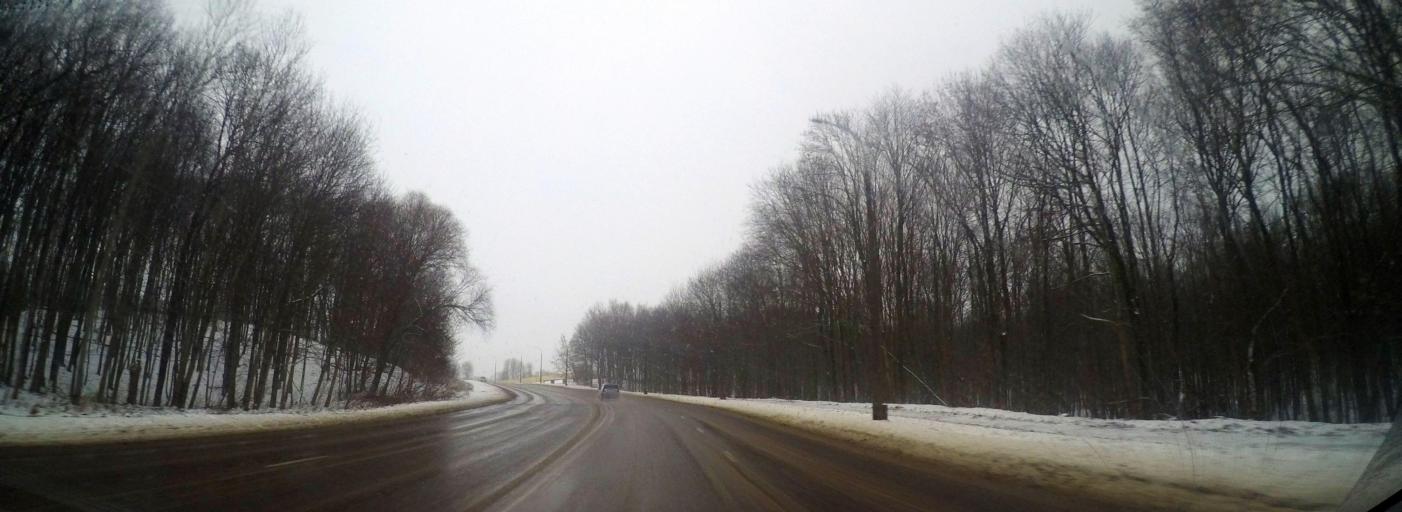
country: BY
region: Grodnenskaya
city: Hrodna
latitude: 53.6794
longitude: 23.8836
